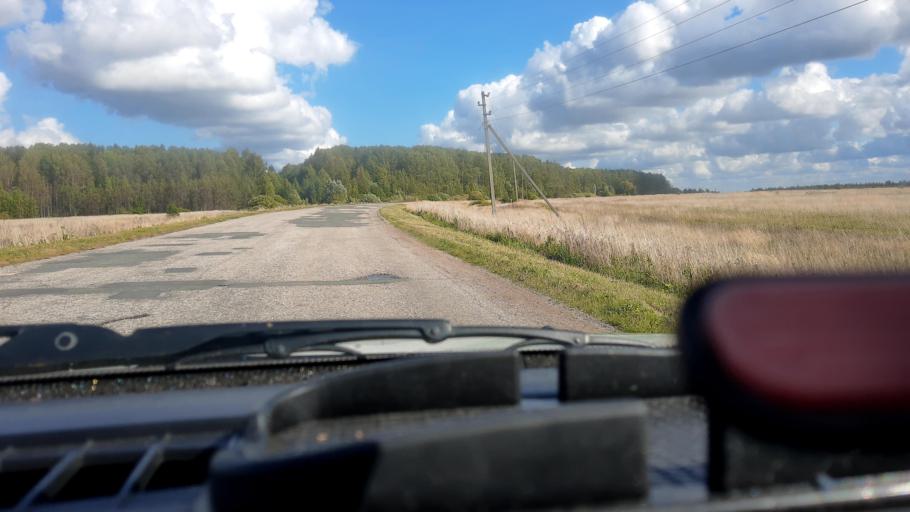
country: RU
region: Mariy-El
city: Kilemary
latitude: 56.9401
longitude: 46.6579
